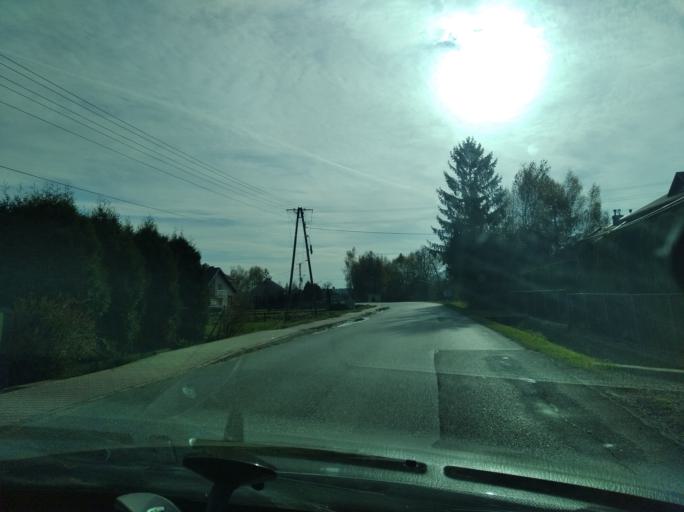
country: PL
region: Subcarpathian Voivodeship
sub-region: Powiat ropczycko-sedziszowski
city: Sedziszow Malopolski
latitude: 50.0826
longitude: 21.6979
